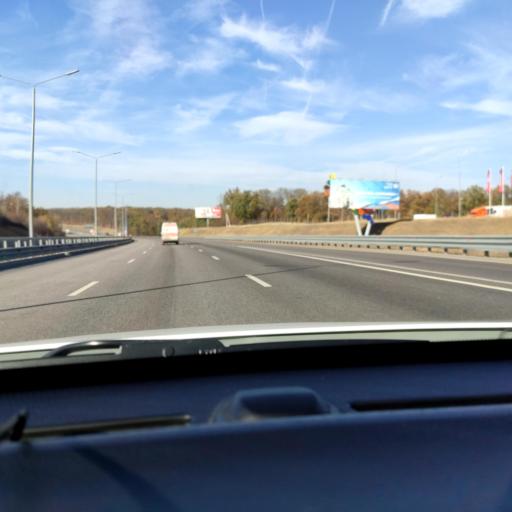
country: RU
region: Voronezj
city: Ramon'
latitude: 51.8246
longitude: 39.2495
